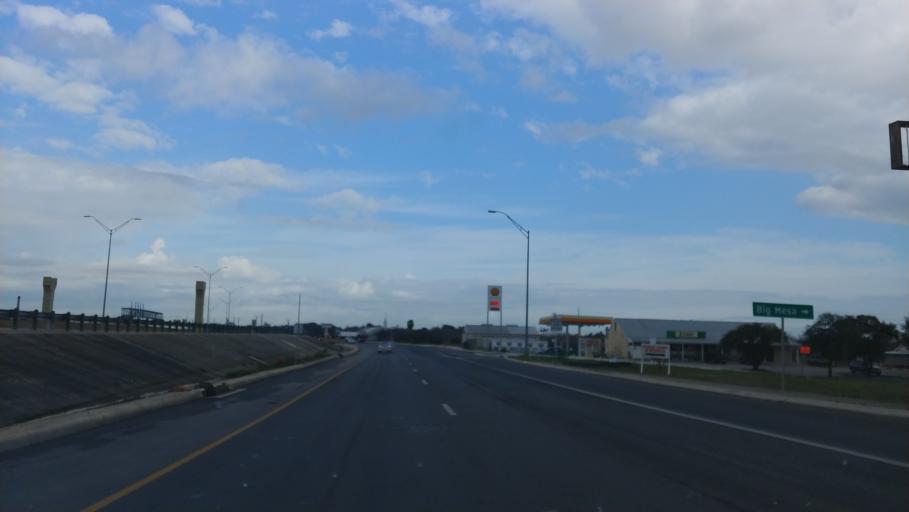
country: US
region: Texas
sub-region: Bexar County
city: Lackland Air Force Base
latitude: 29.3945
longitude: -98.7022
